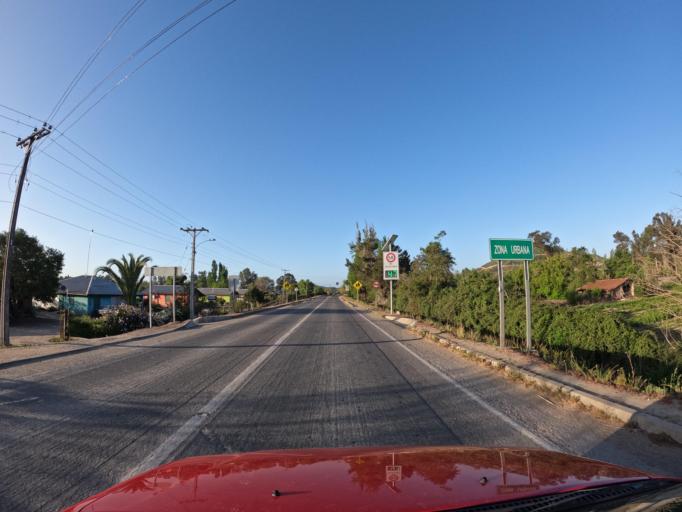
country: CL
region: O'Higgins
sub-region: Provincia de Colchagua
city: Santa Cruz
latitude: -34.3592
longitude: -71.4127
